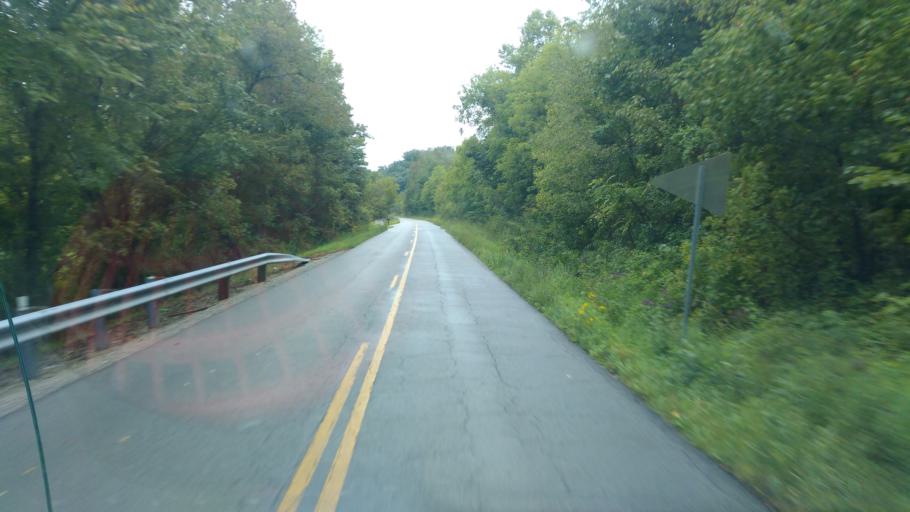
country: US
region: Kentucky
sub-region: Fleming County
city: Flemingsburg
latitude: 38.4332
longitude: -83.4990
